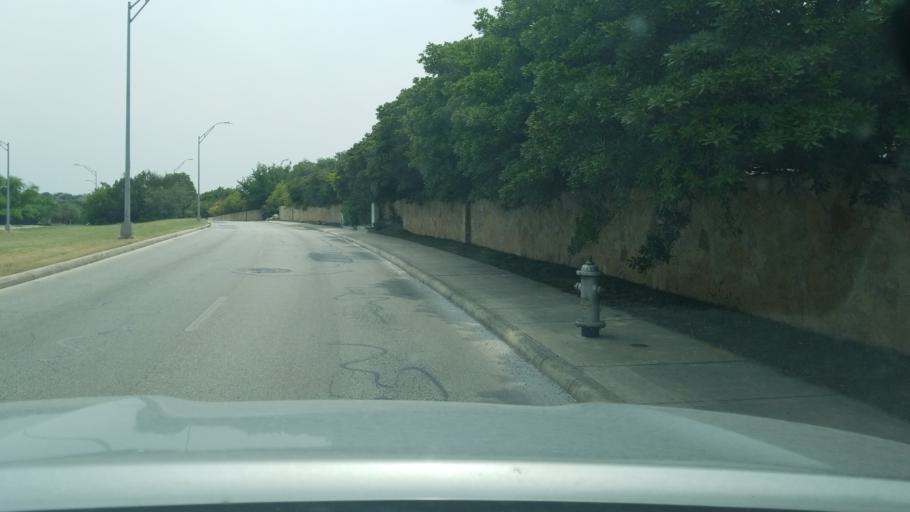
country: US
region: Texas
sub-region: Bexar County
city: Hollywood Park
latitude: 29.6452
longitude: -98.4362
